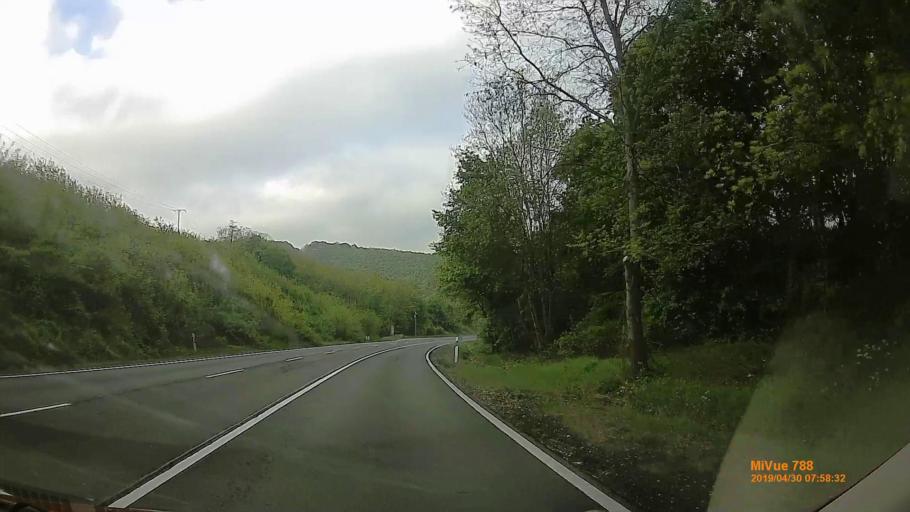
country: HU
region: Nograd
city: Retsag
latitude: 47.8691
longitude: 19.1097
